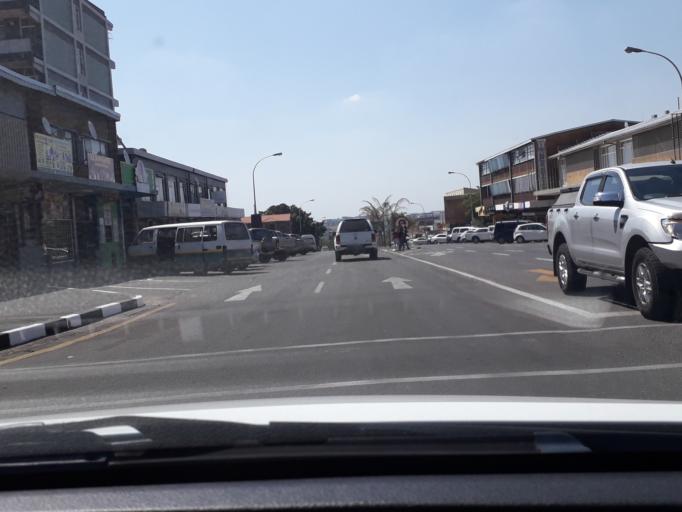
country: ZA
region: Gauteng
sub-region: City of Johannesburg Metropolitan Municipality
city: Modderfontein
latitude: -26.1432
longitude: 28.1540
